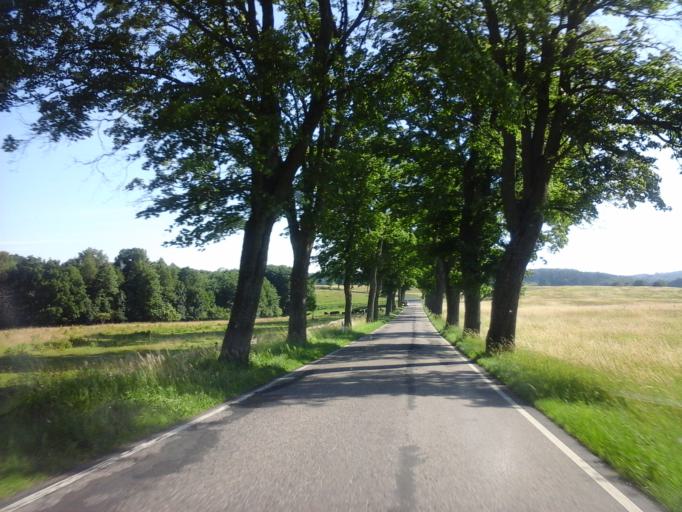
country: PL
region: West Pomeranian Voivodeship
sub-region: Powiat drawski
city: Zlocieniec
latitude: 53.6071
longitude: 15.9167
